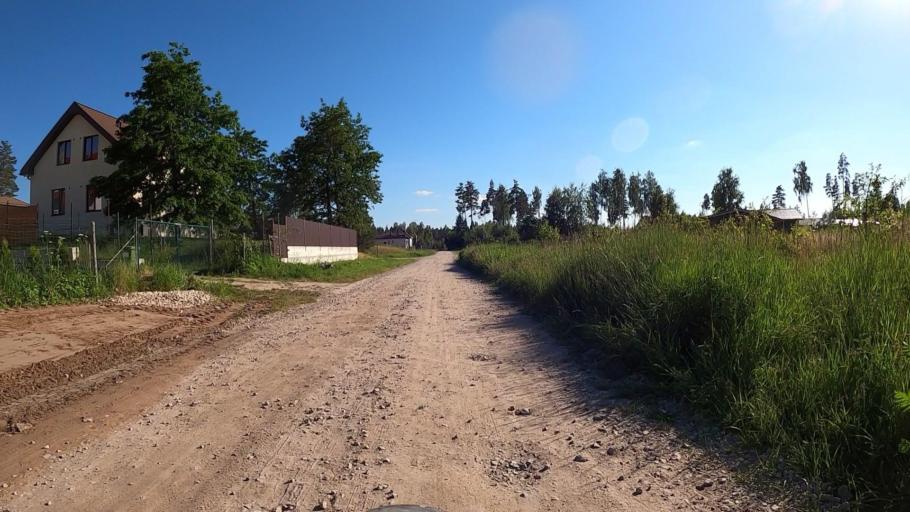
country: LV
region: Stopini
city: Ulbroka
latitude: 56.8812
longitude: 24.2980
